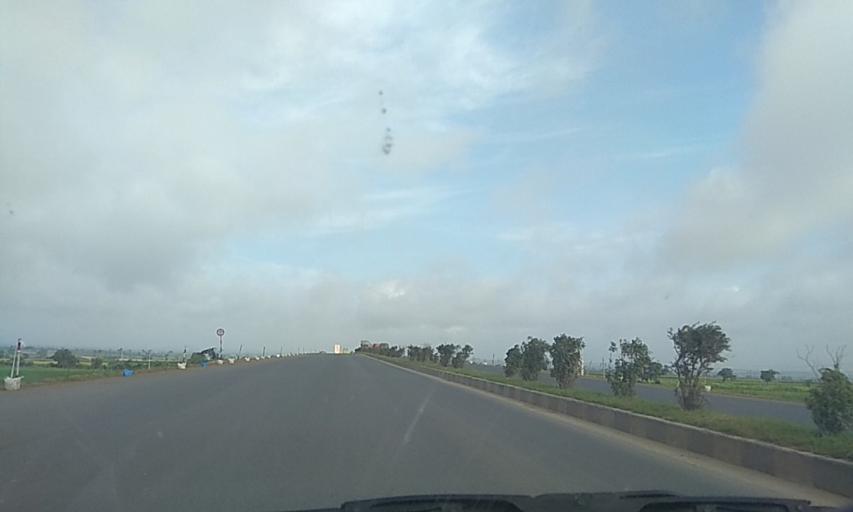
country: IN
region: Karnataka
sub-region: Haveri
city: Haveri
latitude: 14.8371
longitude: 75.3551
